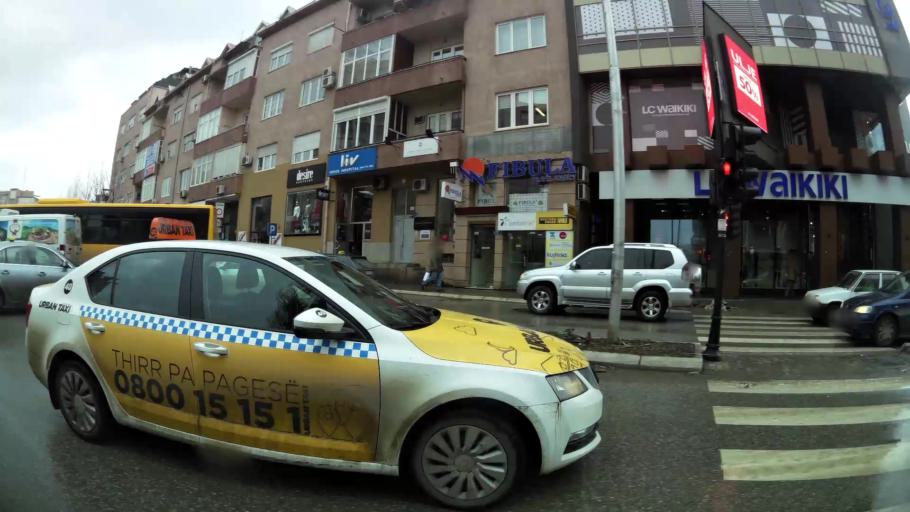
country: XK
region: Pristina
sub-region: Komuna e Prishtines
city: Pristina
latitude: 42.6591
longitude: 21.1605
